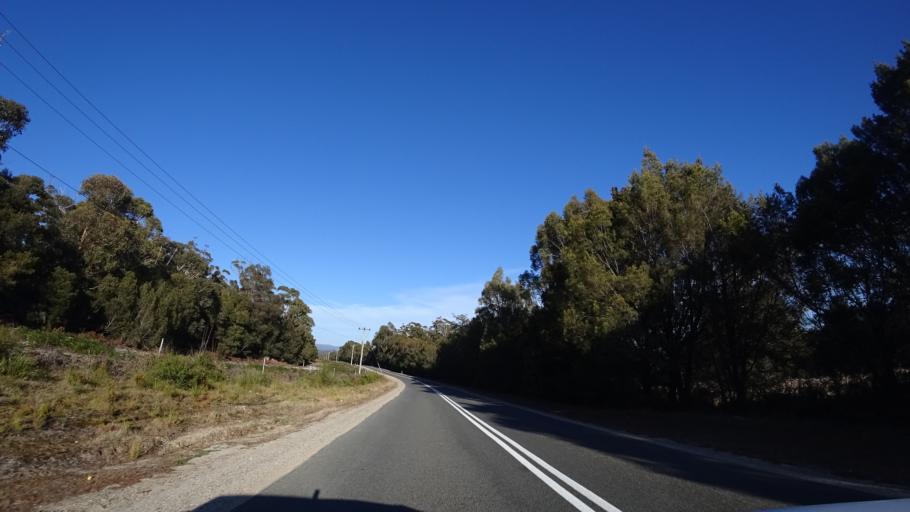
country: AU
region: Tasmania
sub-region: Break O'Day
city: St Helens
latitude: -41.2955
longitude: 148.1957
